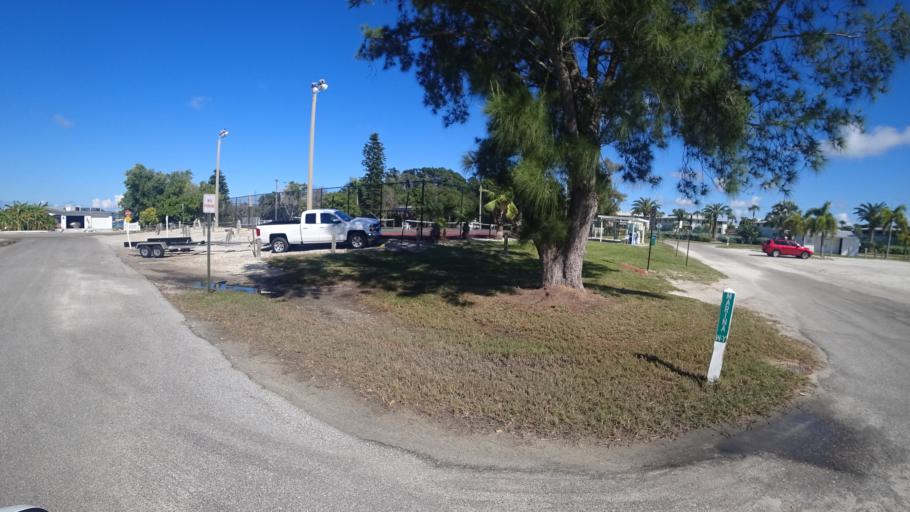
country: US
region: Florida
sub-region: Manatee County
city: Holmes Beach
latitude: 27.5126
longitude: -82.7143
